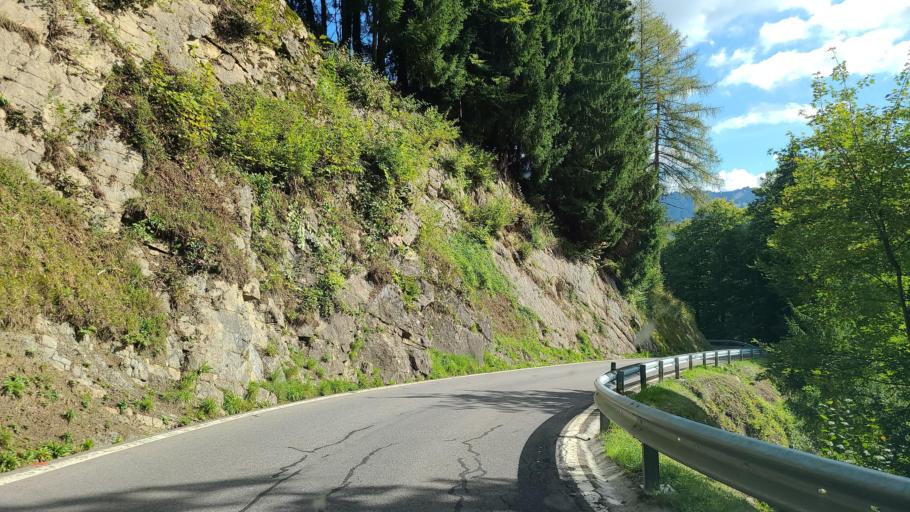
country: CH
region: Schwyz
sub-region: Bezirk March
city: Vorderthal
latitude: 47.1323
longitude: 8.8795
